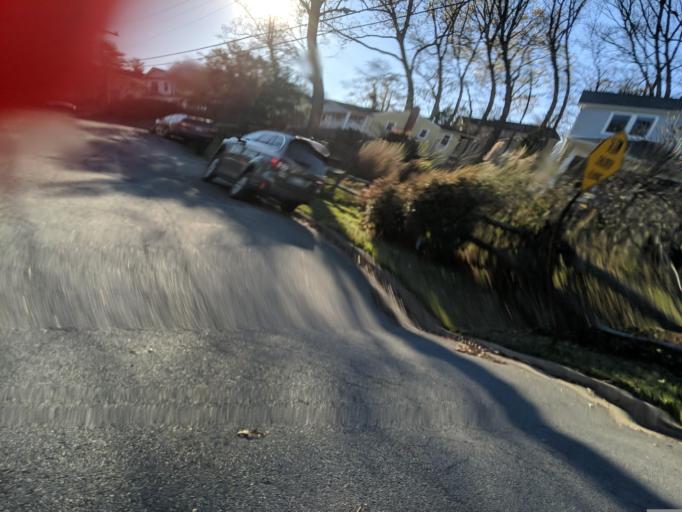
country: US
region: Virginia
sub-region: Fairfax County
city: Vienna
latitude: 38.8936
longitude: -77.2538
